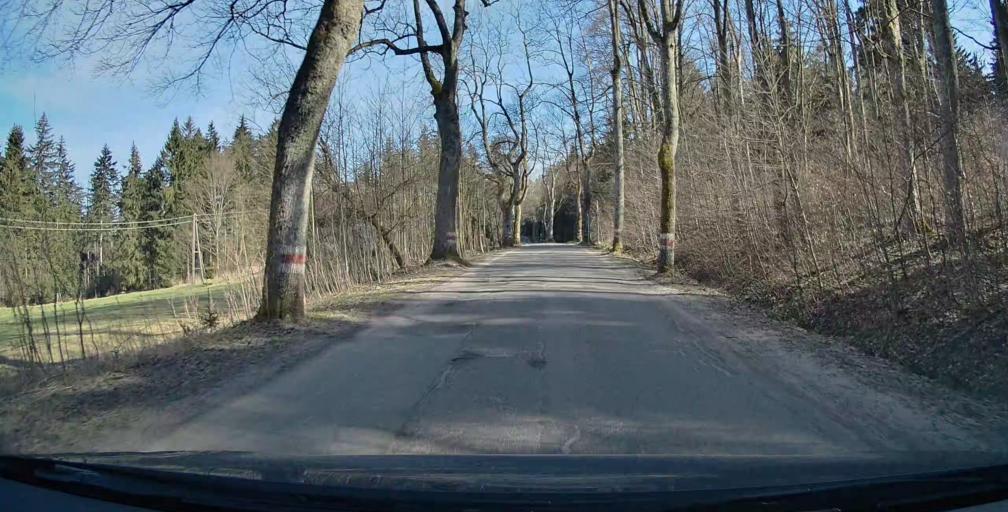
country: PL
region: Lower Silesian Voivodeship
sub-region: Powiat klodzki
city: Radkow
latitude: 50.4687
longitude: 16.3428
